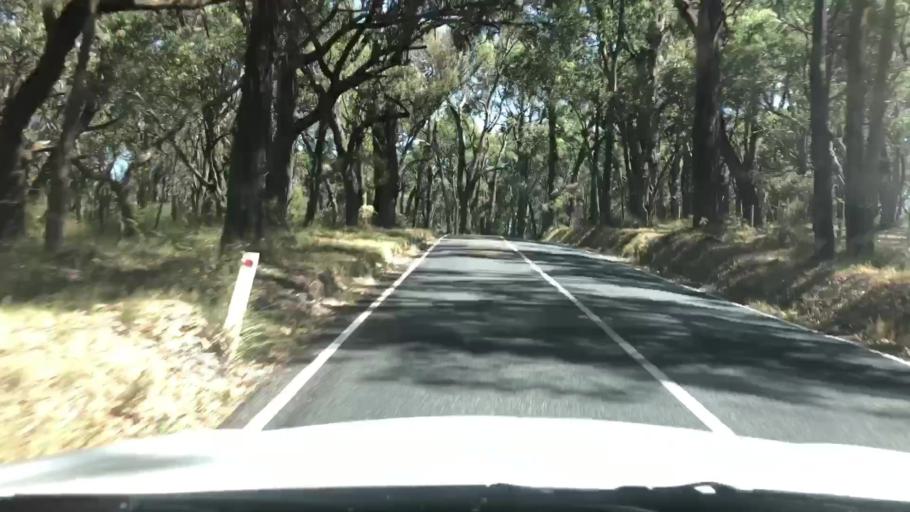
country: AU
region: Victoria
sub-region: Yarra Ranges
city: Macclesfield
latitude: -37.8551
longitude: 145.4831
